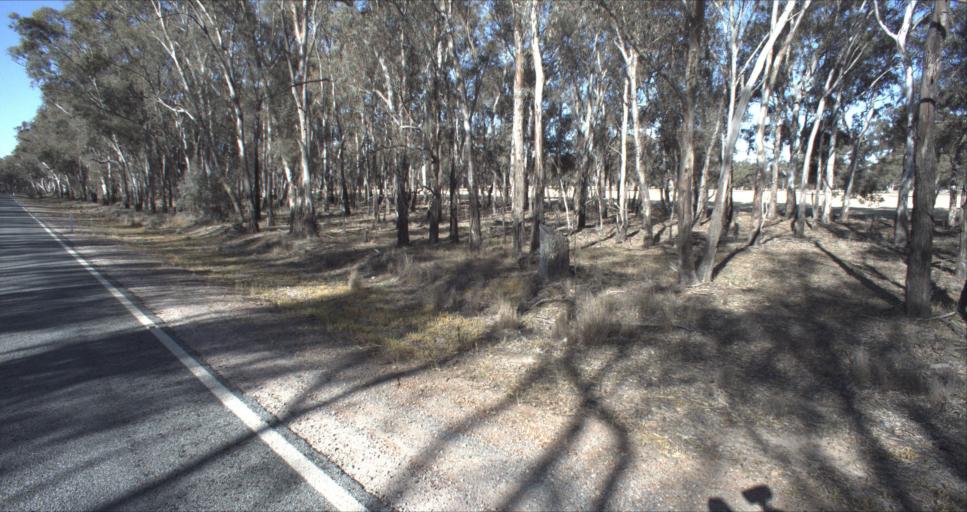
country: AU
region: New South Wales
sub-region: Leeton
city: Leeton
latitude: -34.6282
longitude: 146.3778
